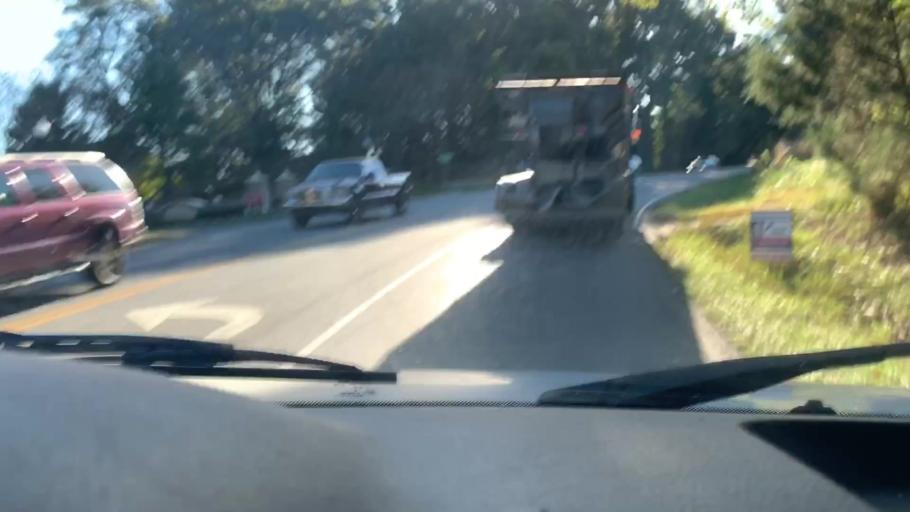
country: US
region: North Carolina
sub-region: Mecklenburg County
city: Huntersville
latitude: 35.4301
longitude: -80.7592
